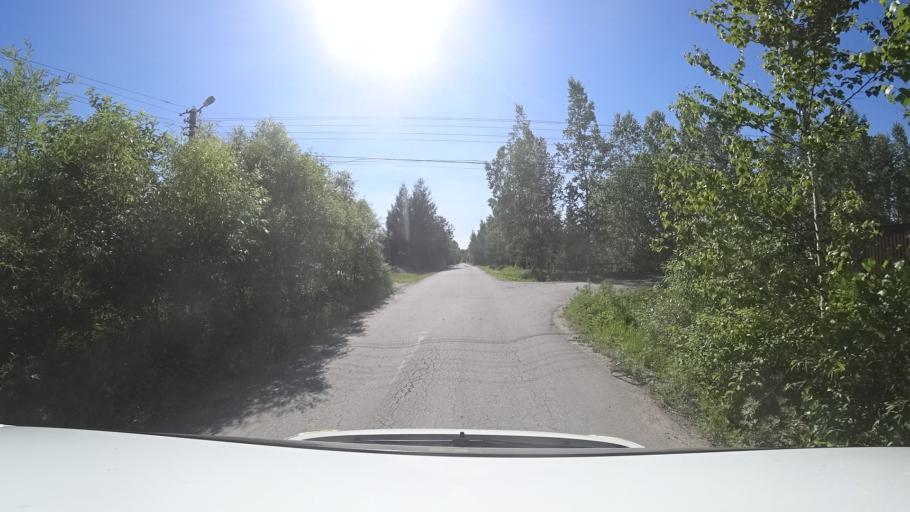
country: RU
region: Khabarovsk Krai
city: Topolevo
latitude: 48.5503
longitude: 135.1728
